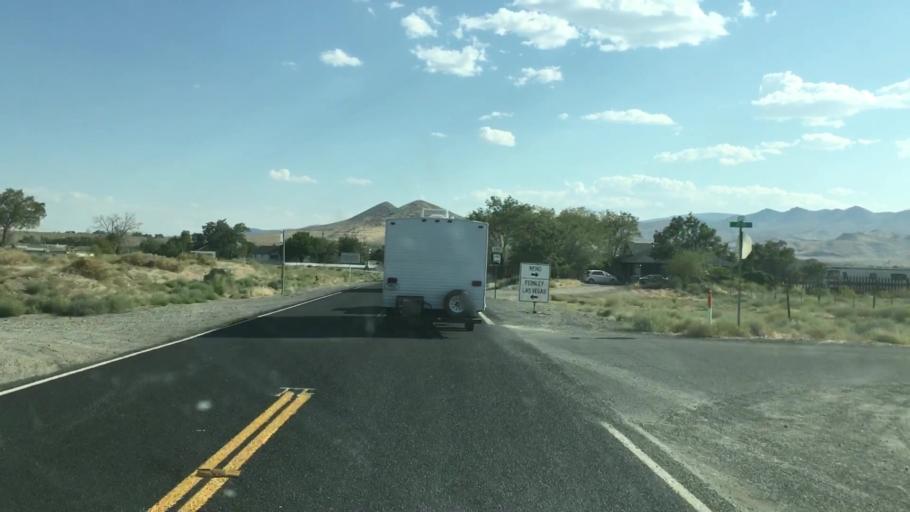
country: US
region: Nevada
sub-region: Lyon County
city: Fernley
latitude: 39.6328
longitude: -119.2906
